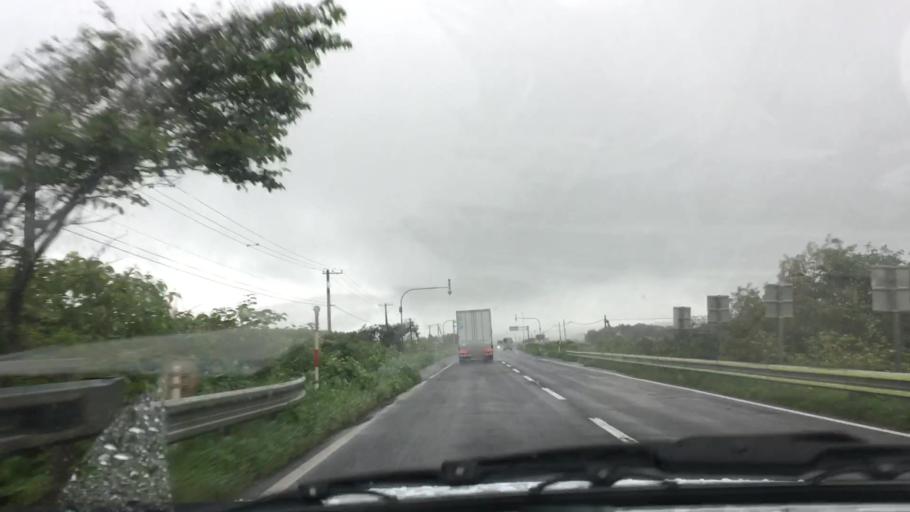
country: JP
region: Hokkaido
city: Niseko Town
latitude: 42.4215
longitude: 140.3133
